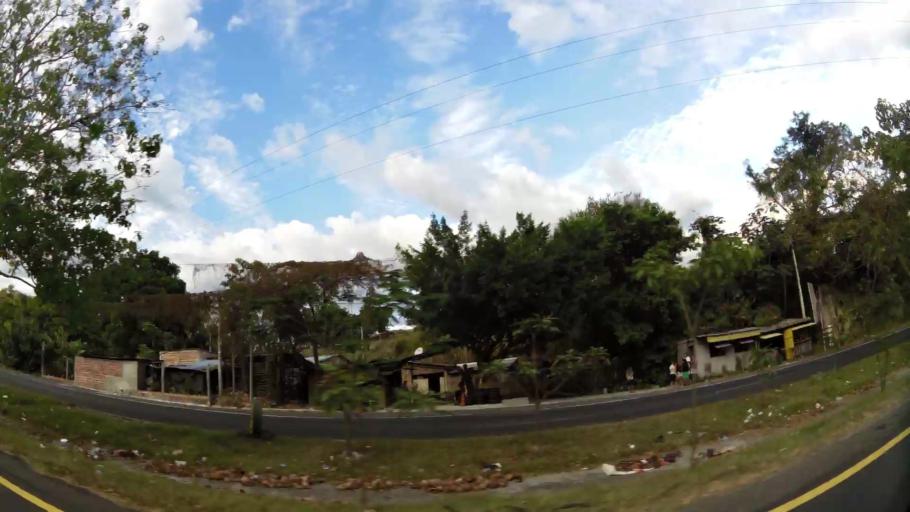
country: SV
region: San Vicente
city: San Sebastian
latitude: 13.7298
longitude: -88.8704
